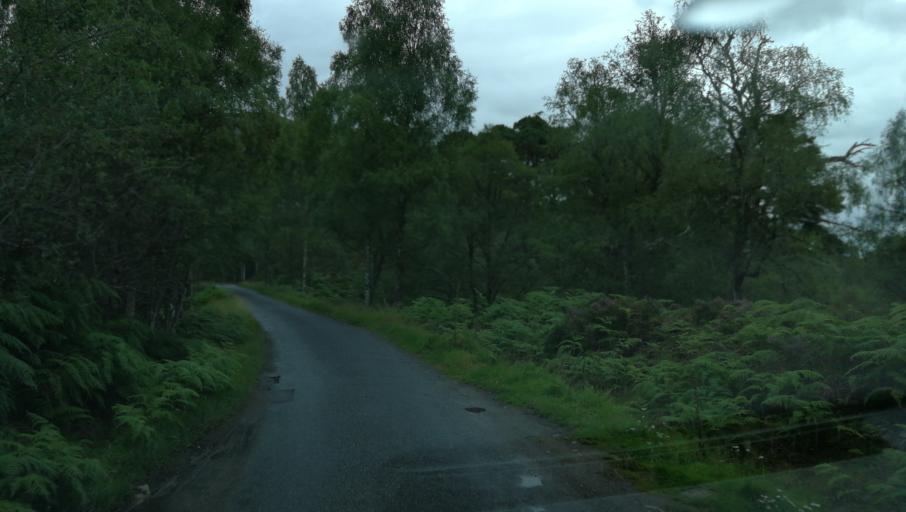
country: GB
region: Scotland
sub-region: Highland
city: Spean Bridge
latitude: 57.2904
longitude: -4.9182
